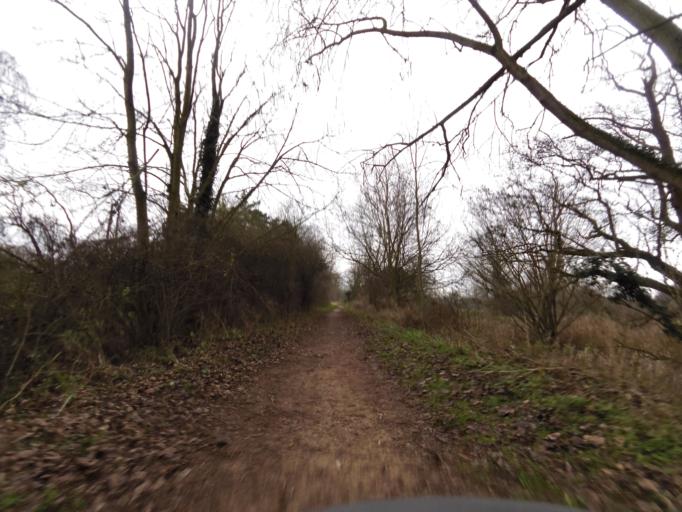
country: GB
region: England
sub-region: Norfolk
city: Mattishall
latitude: 52.7424
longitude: 1.0941
